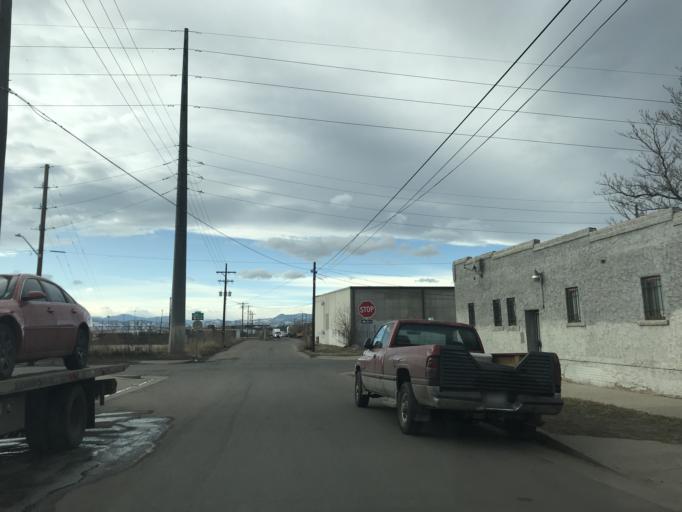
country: US
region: Colorado
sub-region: Adams County
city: Commerce City
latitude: 39.7763
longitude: -104.9583
